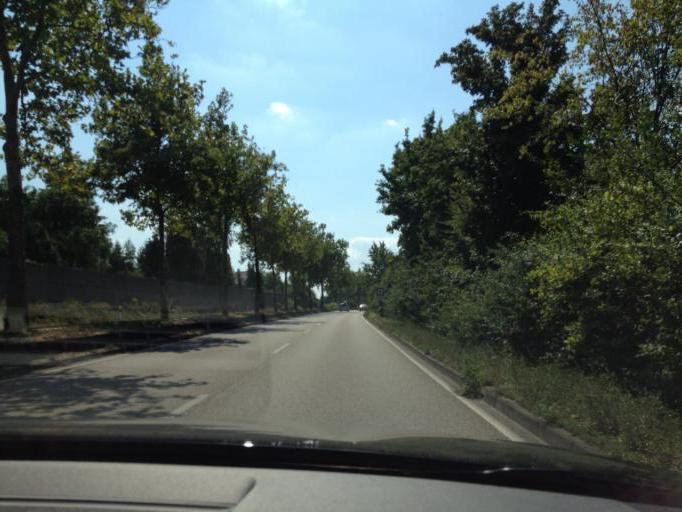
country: DE
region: Baden-Wuerttemberg
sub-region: Regierungsbezirk Stuttgart
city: Heilbronn
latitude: 49.1618
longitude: 9.2262
